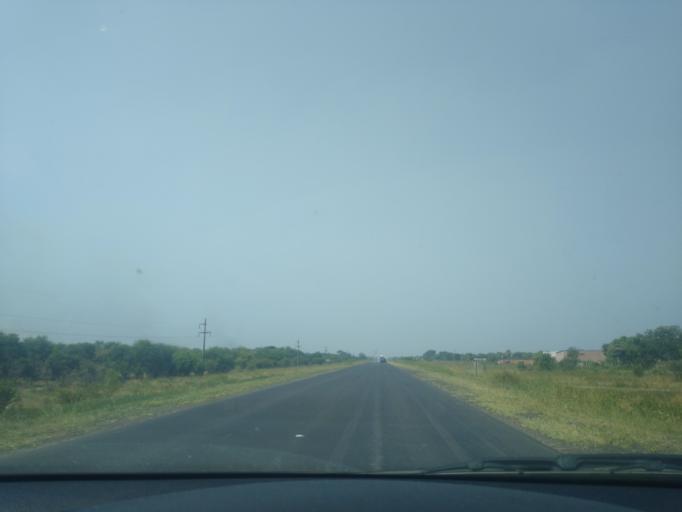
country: AR
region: Chaco
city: Fontana
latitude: -27.4960
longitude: -59.0793
